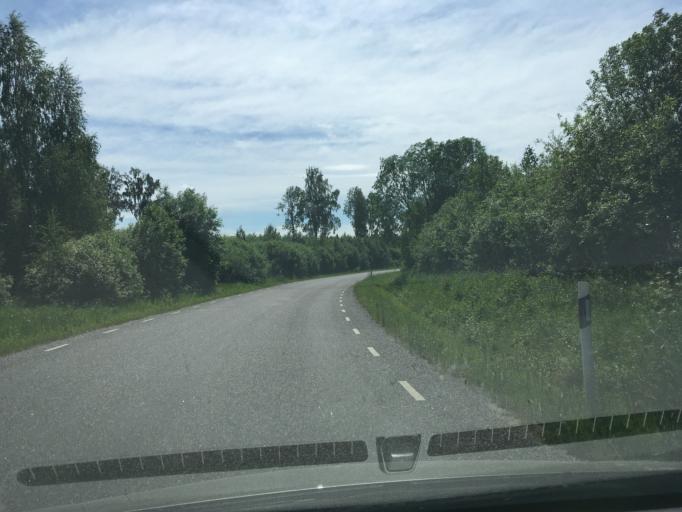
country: EE
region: Paernumaa
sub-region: Audru vald
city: Audru
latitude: 58.4531
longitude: 24.3897
